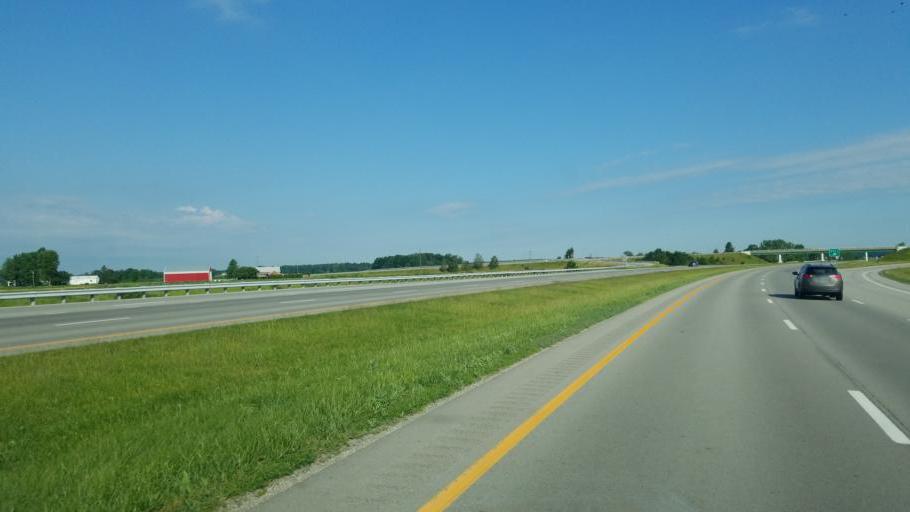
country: US
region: Ohio
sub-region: Wyandot County
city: Carey
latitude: 40.9671
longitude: -83.4808
